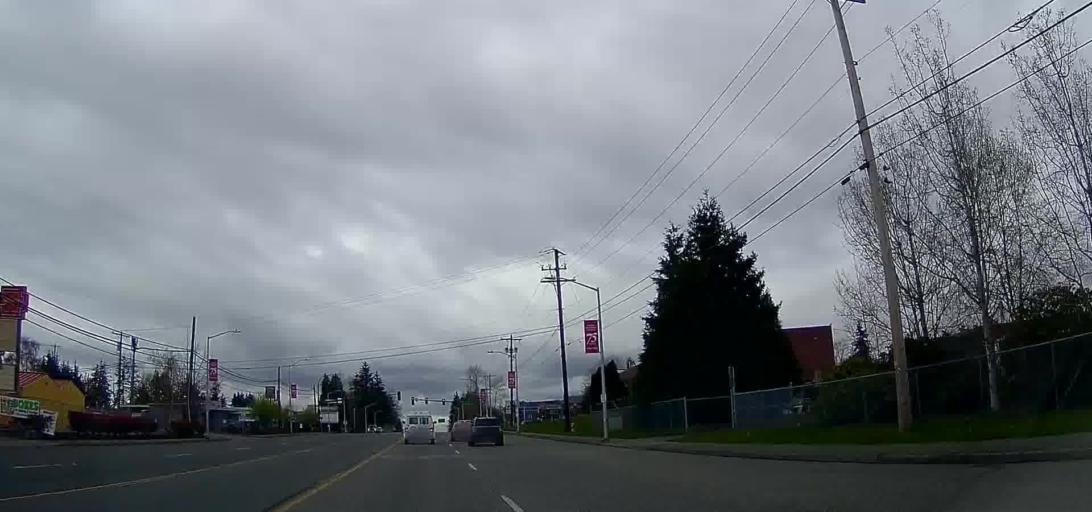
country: US
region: Washington
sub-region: Snohomish County
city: Everett
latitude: 48.0069
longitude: -122.1957
